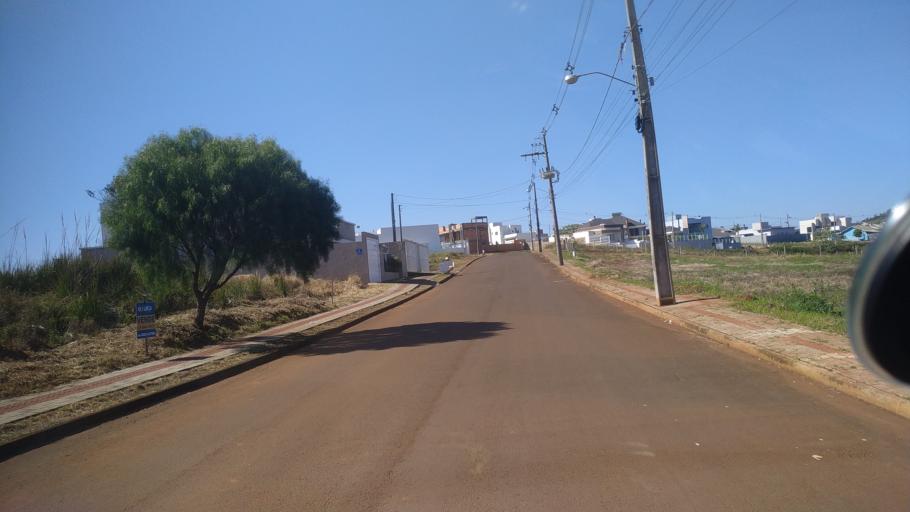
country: BR
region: Santa Catarina
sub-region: Chapeco
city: Chapeco
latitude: -27.0884
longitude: -52.5834
